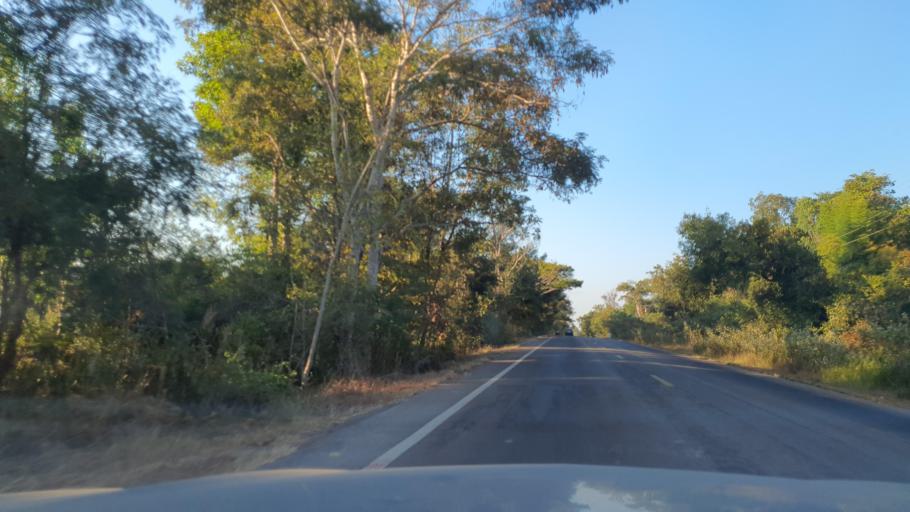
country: TH
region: Nakhon Phanom
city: Si Songkhram
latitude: 17.5554
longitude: 104.2392
